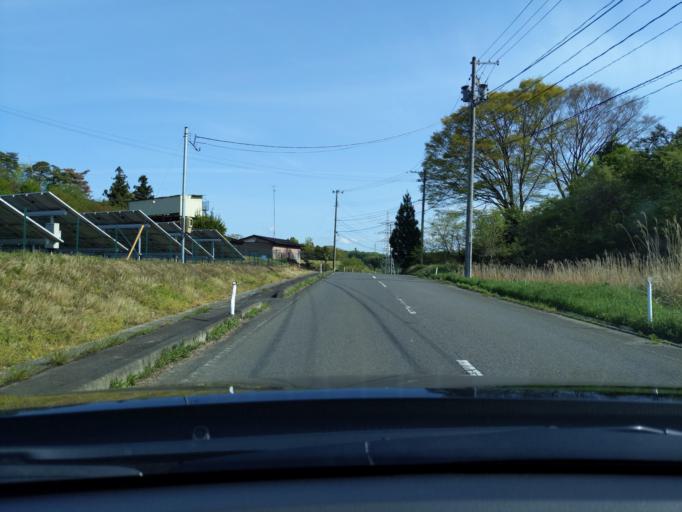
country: JP
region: Fukushima
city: Sukagawa
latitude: 37.3039
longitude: 140.4243
